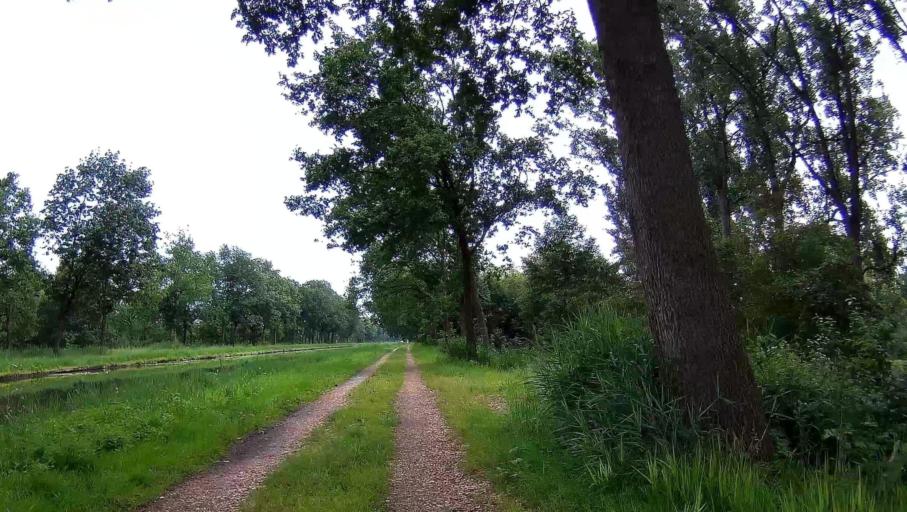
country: BE
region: Flanders
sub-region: Provincie Limburg
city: Leopoldsburg
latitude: 51.1880
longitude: 5.2512
